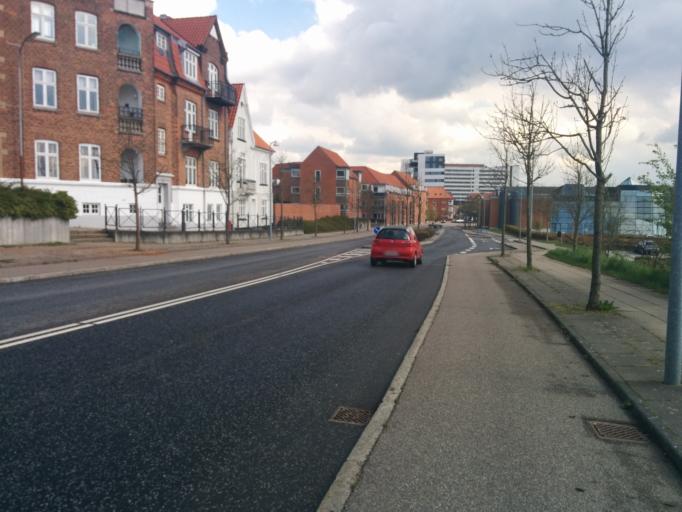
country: DK
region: Central Jutland
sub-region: Viborg Kommune
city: Viborg
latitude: 56.4490
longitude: 9.3961
